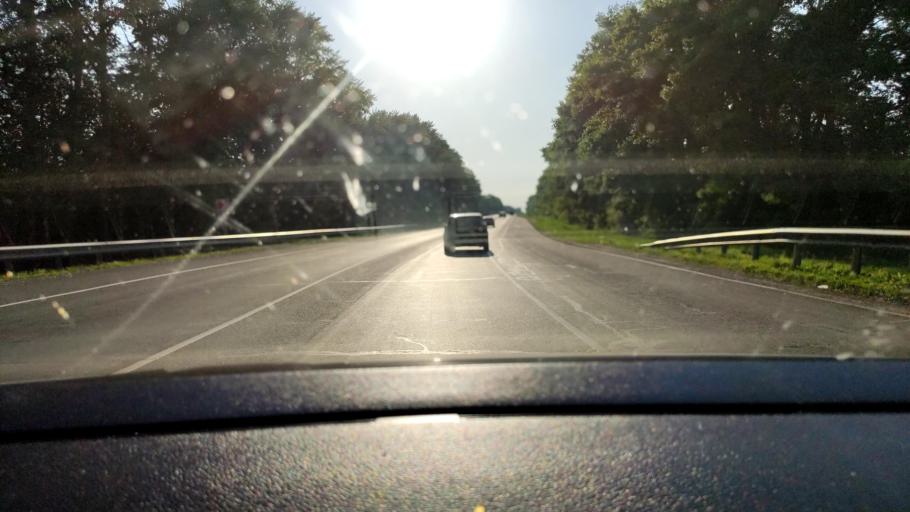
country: RU
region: Voronezj
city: Kashirskoye
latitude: 51.4927
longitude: 39.6091
